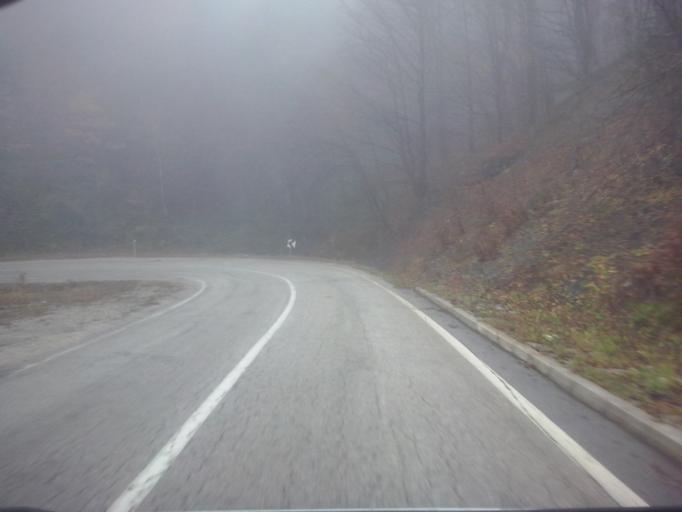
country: RS
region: Central Serbia
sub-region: Moravicki Okrug
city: Ivanjica
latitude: 43.5356
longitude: 20.3072
